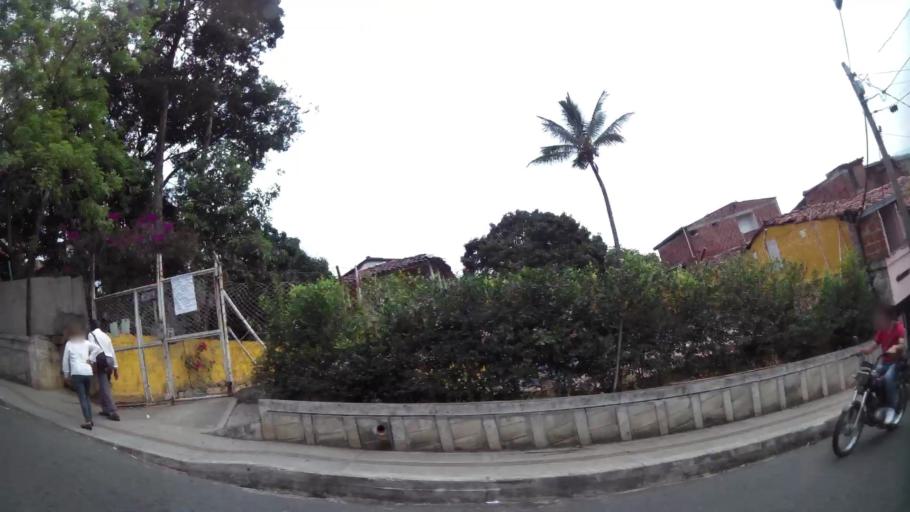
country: CO
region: Antioquia
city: Bello
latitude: 6.3004
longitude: -75.5544
